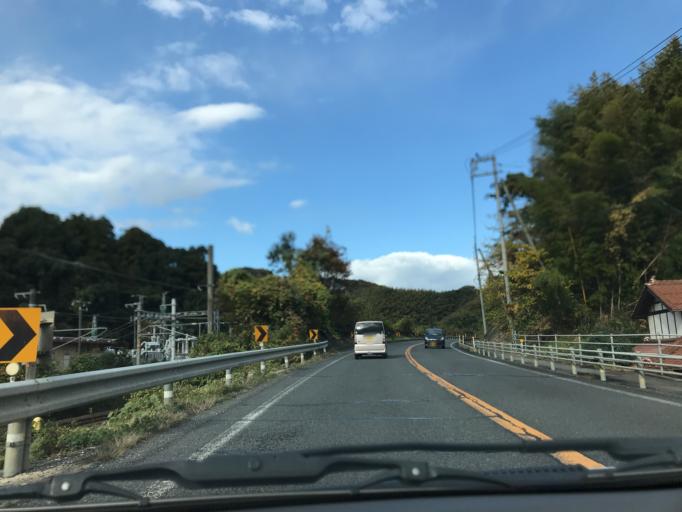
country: JP
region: Tottori
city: Yonago
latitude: 35.4084
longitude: 133.2982
